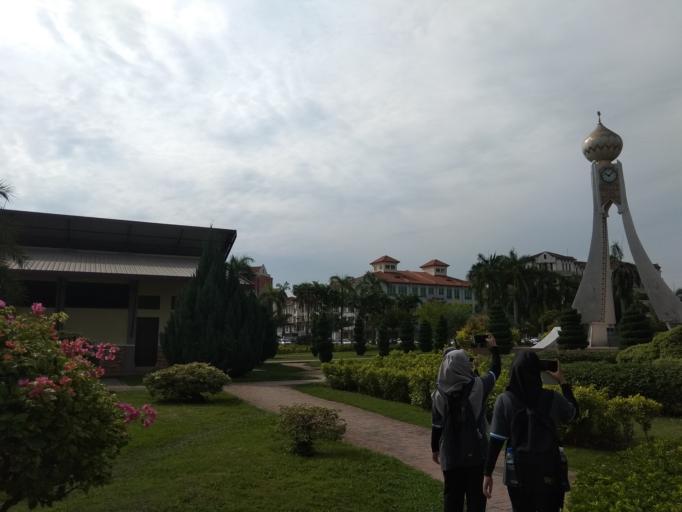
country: MY
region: Perak
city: Ipoh
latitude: 4.5996
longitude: 101.0907
